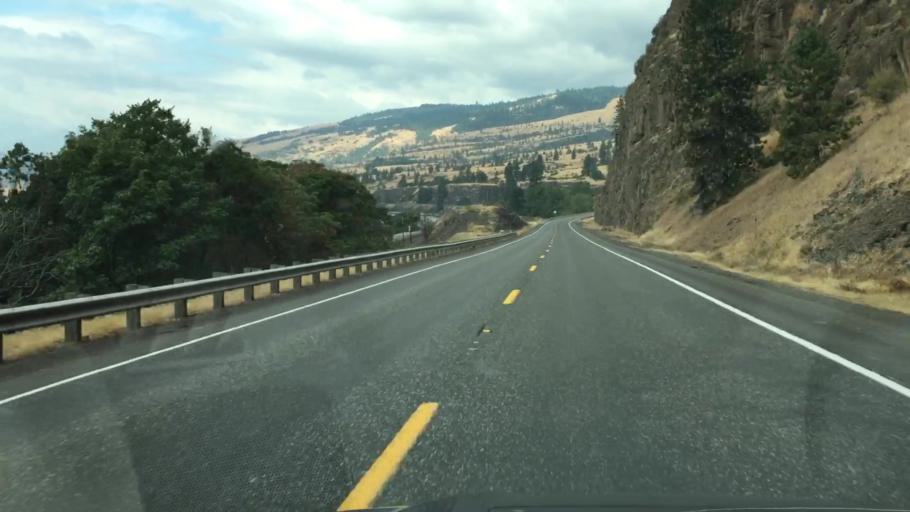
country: US
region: Oregon
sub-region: Wasco County
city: Chenoweth
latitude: 45.7086
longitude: -121.3359
